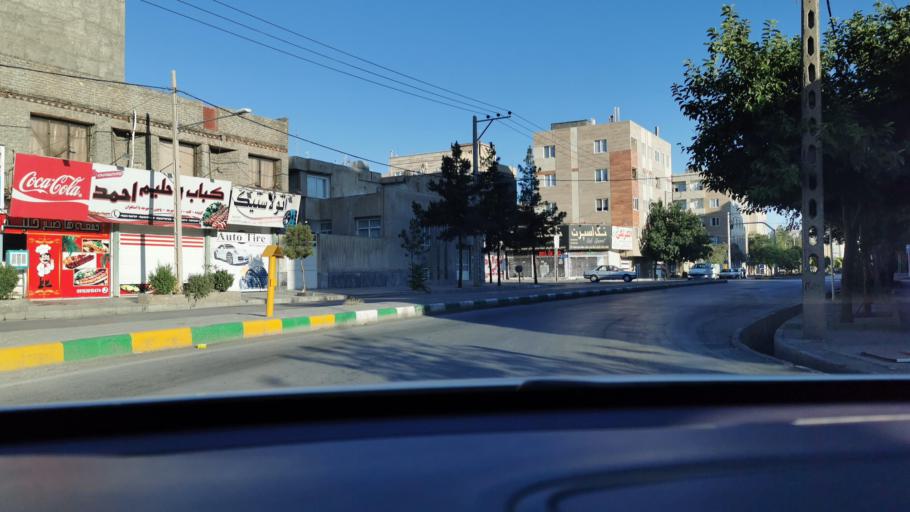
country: IR
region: Razavi Khorasan
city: Mashhad
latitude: 36.3566
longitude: 59.4873
